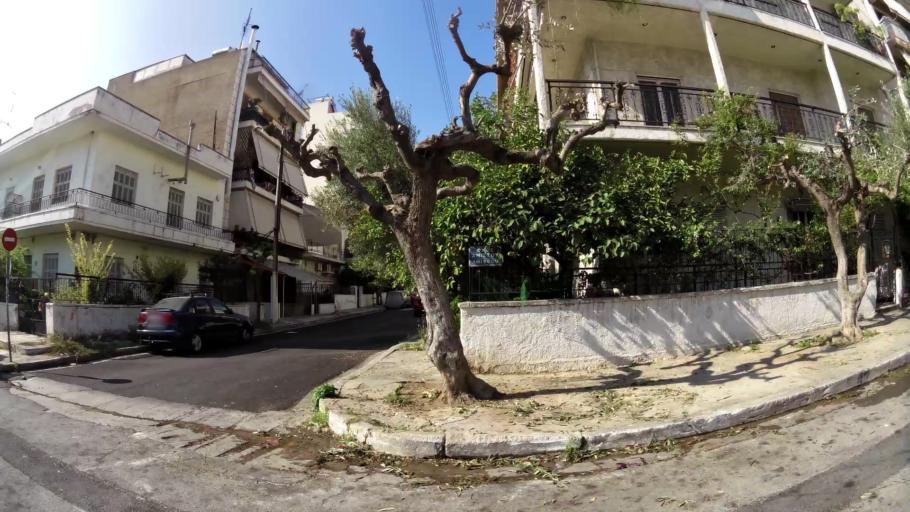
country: GR
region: Attica
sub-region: Nomos Piraios
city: Keratsini
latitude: 37.9658
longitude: 23.6171
